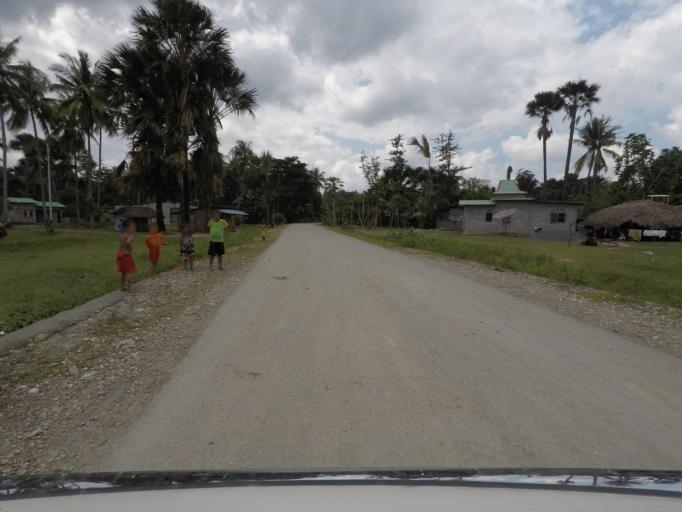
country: TL
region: Viqueque
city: Viqueque
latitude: -8.8836
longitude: 126.3740
